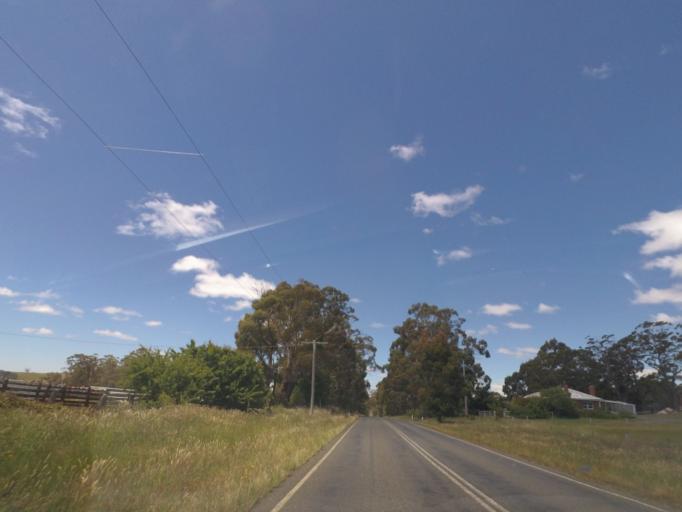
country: AU
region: Victoria
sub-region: Mount Alexander
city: Castlemaine
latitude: -37.3191
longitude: 144.2095
